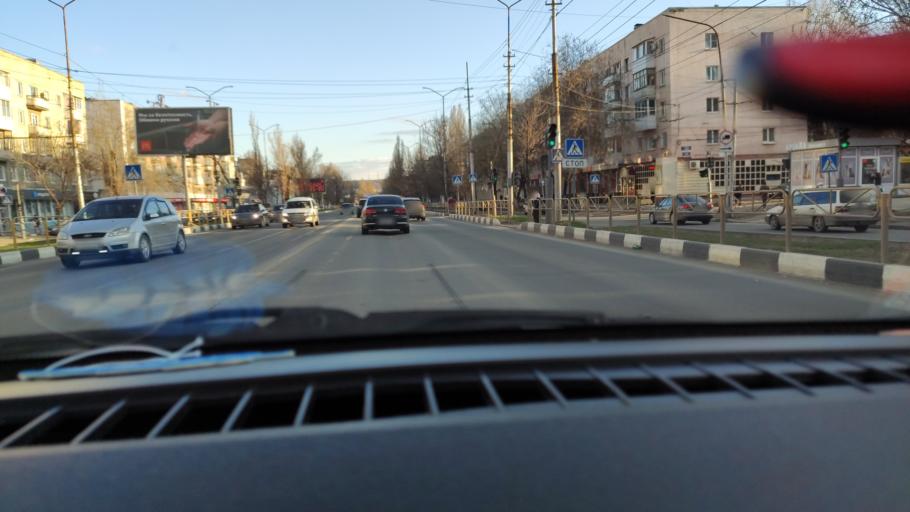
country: RU
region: Saratov
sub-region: Saratovskiy Rayon
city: Saratov
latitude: 51.5967
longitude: 45.9682
